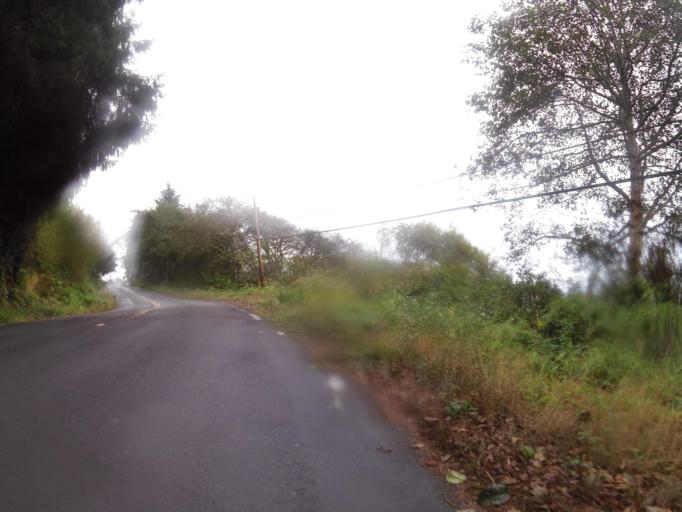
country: US
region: California
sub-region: Humboldt County
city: Westhaven-Moonstone
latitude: 41.1026
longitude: -124.1598
